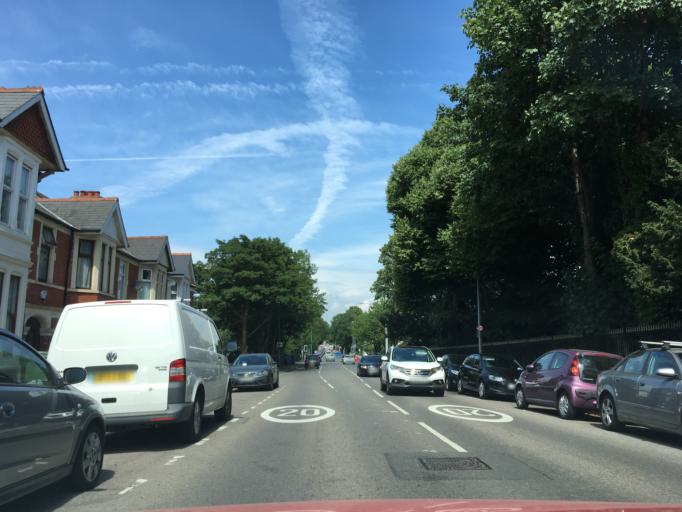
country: GB
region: Wales
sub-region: Cardiff
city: Cardiff
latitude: 51.5028
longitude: -3.1836
